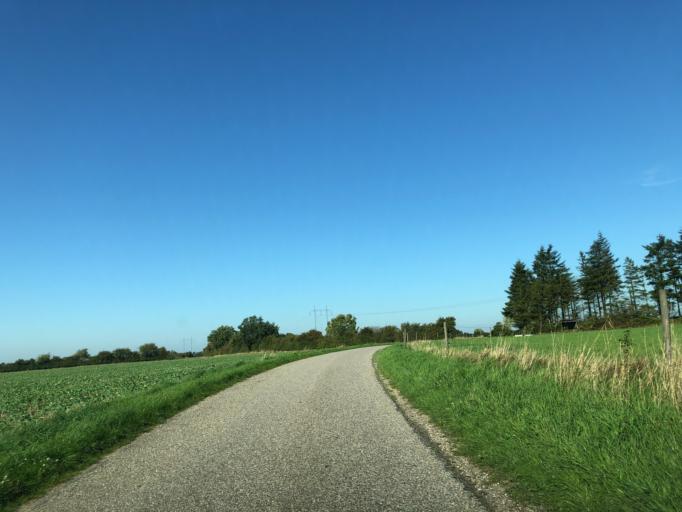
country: DK
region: South Denmark
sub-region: Sonderborg Kommune
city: Dybbol
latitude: 54.9370
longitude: 9.7303
